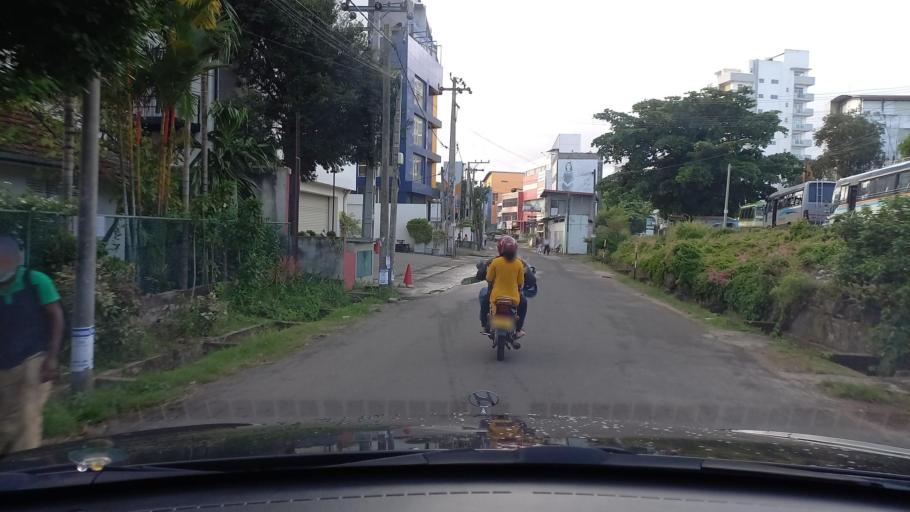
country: LK
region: Western
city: Sri Jayewardenepura Kotte
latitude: 6.8734
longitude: 79.8885
